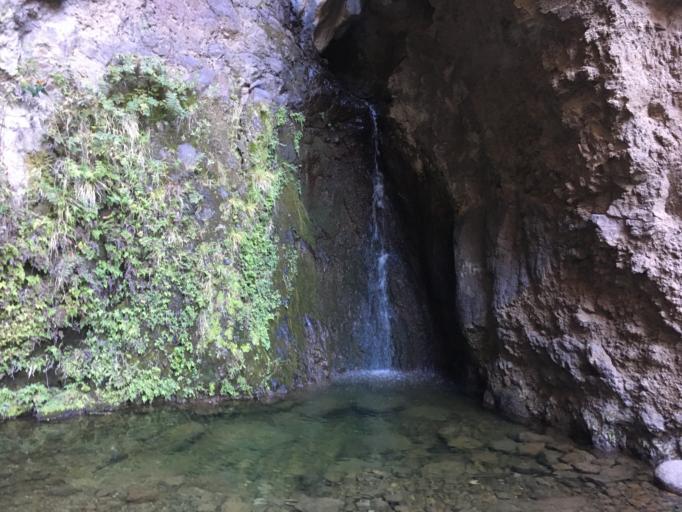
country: ES
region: Canary Islands
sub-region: Provincia de Santa Cruz de Tenerife
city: Vilaflor
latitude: 28.2008
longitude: -16.5813
